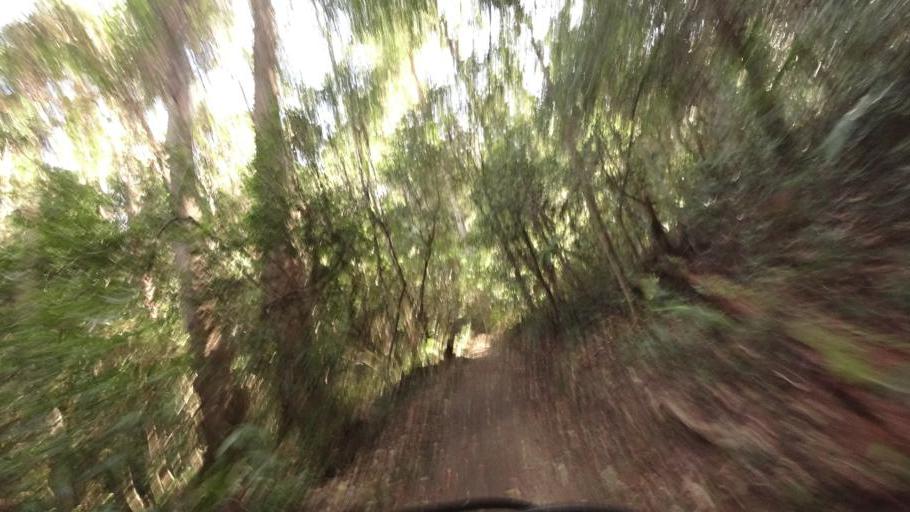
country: AU
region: Queensland
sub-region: Moreton Bay
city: Highvale
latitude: -27.4023
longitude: 152.8007
